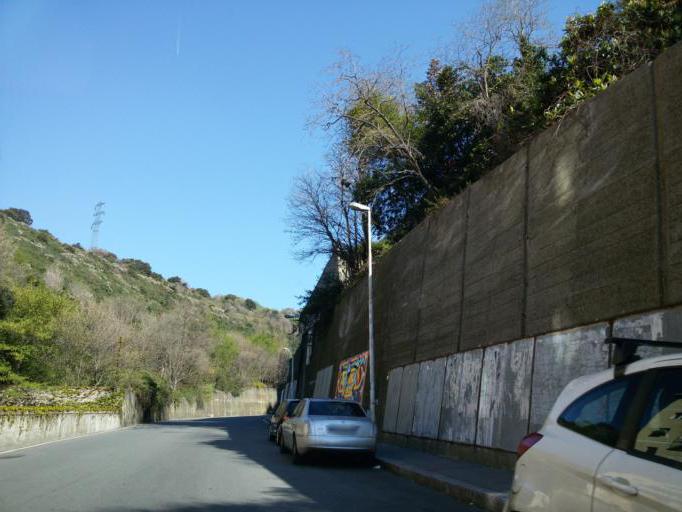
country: IT
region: Liguria
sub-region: Provincia di Genova
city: San Teodoro
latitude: 44.4221
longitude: 8.9088
